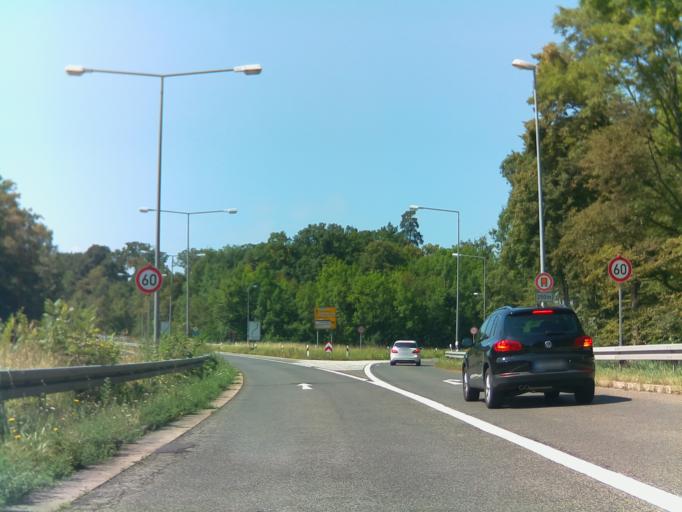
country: DE
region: Baden-Wuerttemberg
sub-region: Regierungsbezirk Stuttgart
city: Gerlingen
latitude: 48.7866
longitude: 9.0692
